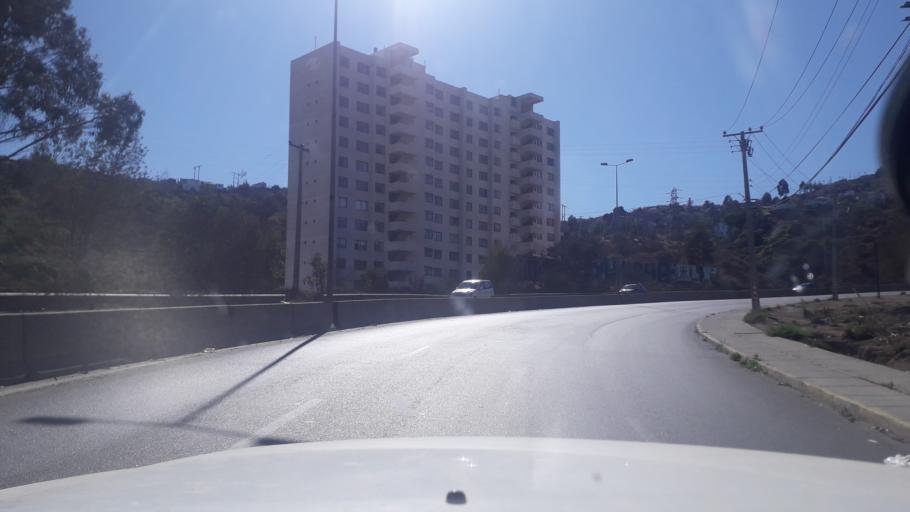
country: CL
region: Valparaiso
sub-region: Provincia de Valparaiso
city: Vina del Mar
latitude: -33.0358
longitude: -71.5163
